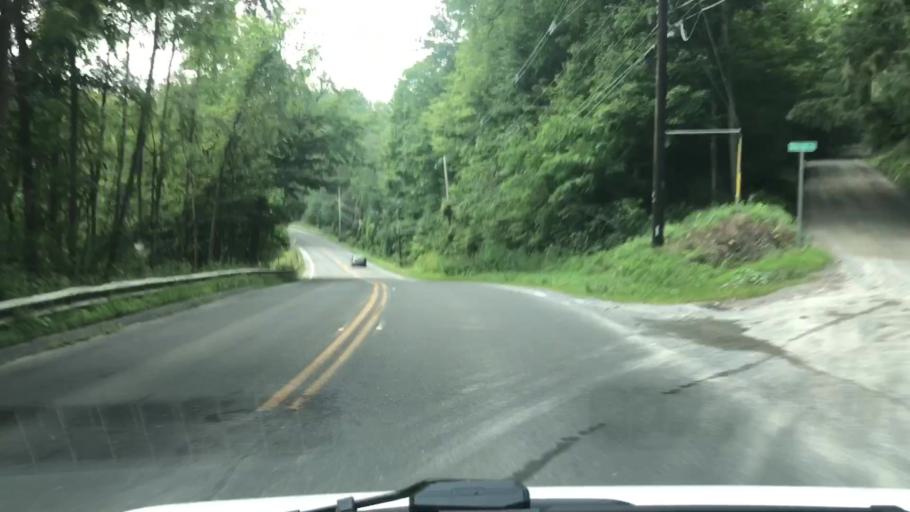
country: US
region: Massachusetts
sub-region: Berkshire County
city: Williamstown
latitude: 42.7098
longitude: -73.2208
